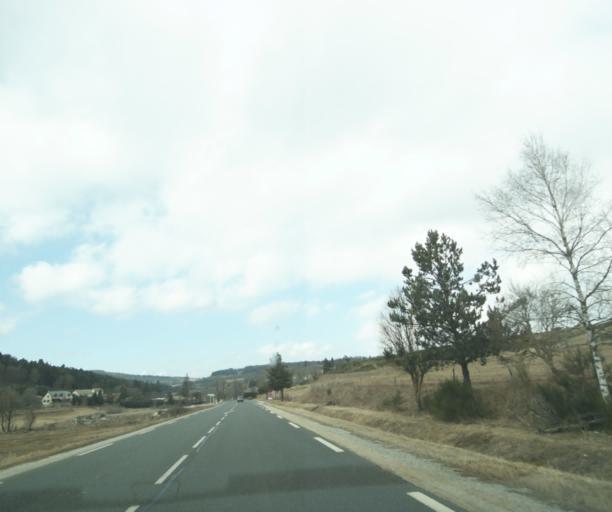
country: FR
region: Languedoc-Roussillon
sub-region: Departement de la Lozere
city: Mende
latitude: 44.5962
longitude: 3.6688
